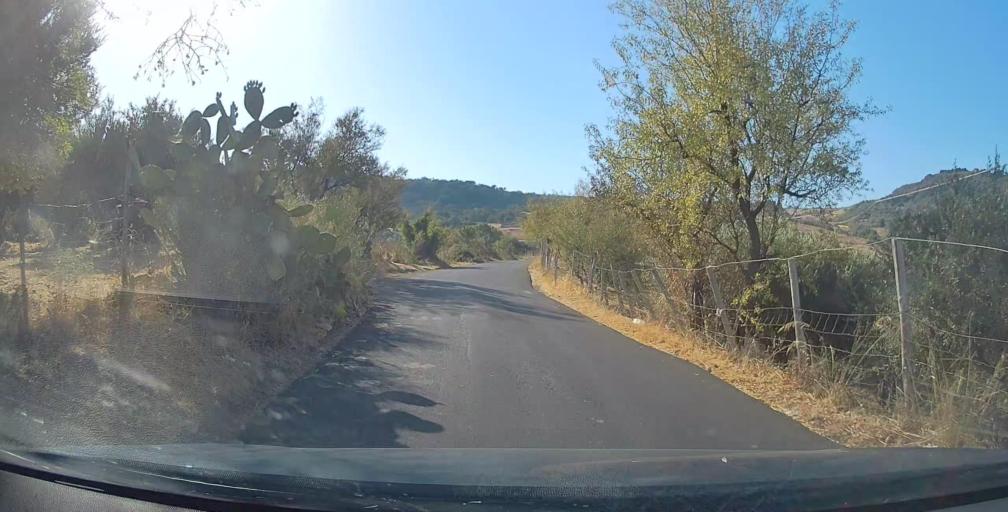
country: IT
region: Sicily
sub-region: Messina
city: San Piero Patti
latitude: 38.0616
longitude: 14.9901
